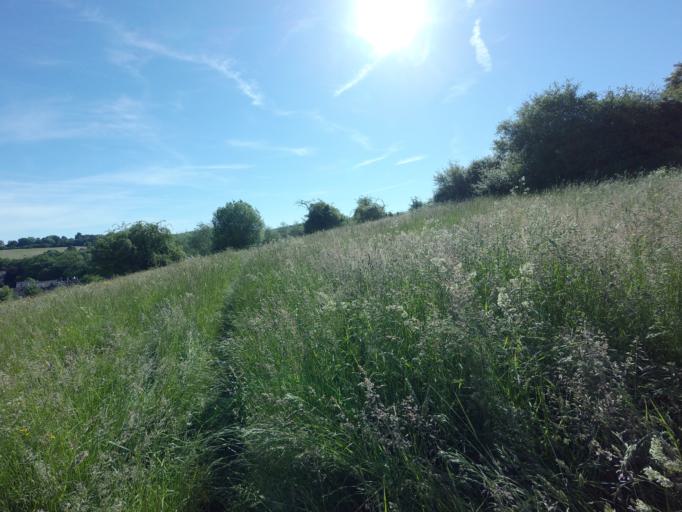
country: NL
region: Limburg
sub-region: Gemeente Simpelveld
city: Simpelveld
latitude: 50.8047
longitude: 5.9561
